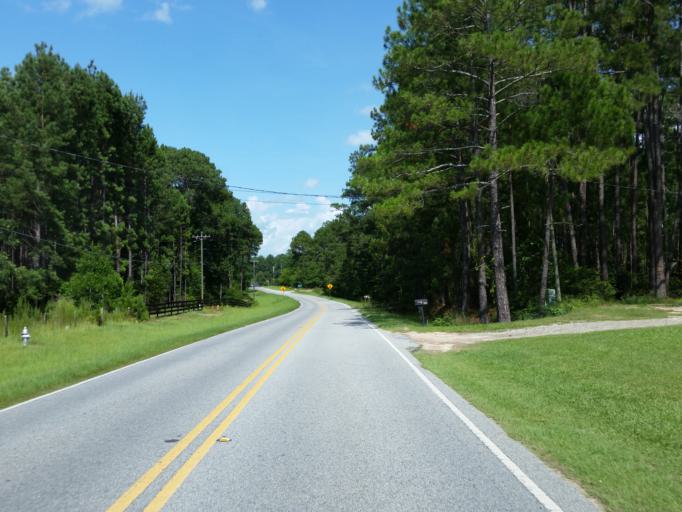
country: US
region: Georgia
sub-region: Tift County
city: Tifton
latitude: 31.5051
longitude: -83.5044
